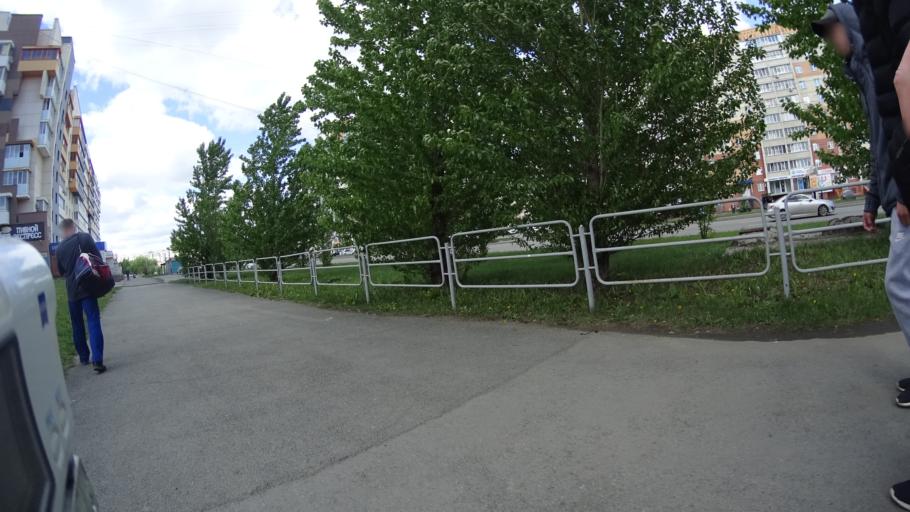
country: RU
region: Chelyabinsk
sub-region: Gorod Chelyabinsk
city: Chelyabinsk
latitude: 55.1655
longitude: 61.2944
